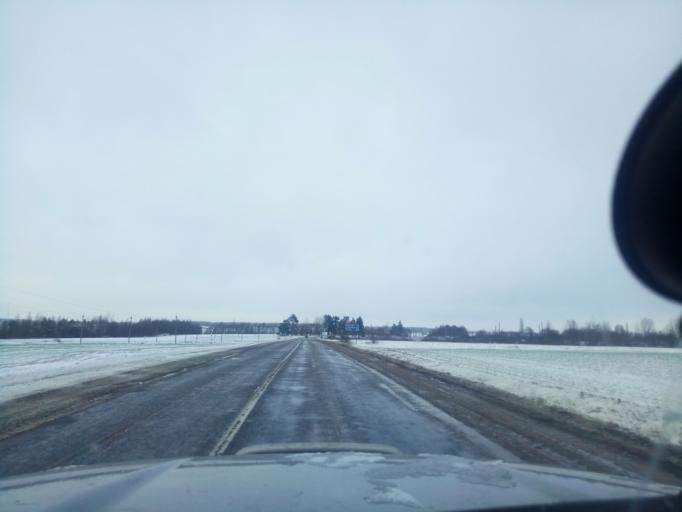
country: BY
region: Minsk
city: Tsimkavichy
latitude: 53.0959
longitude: 27.0386
